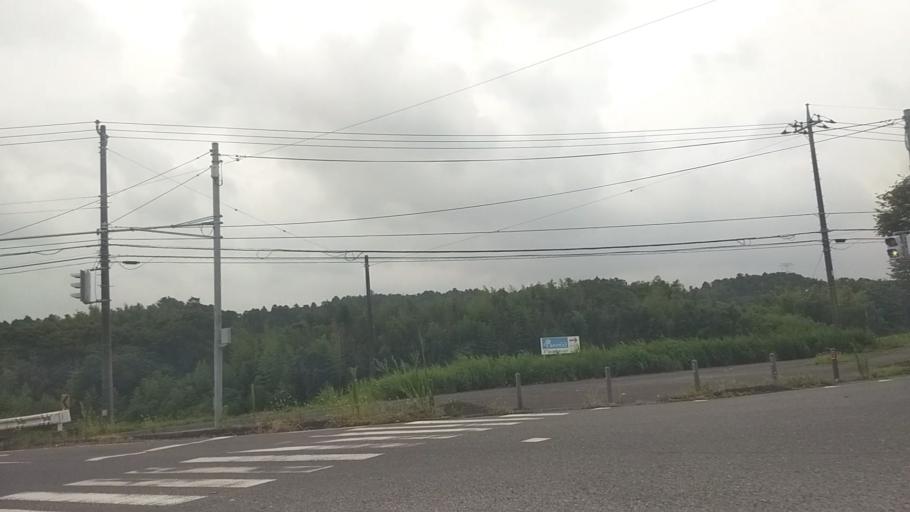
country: JP
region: Chiba
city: Kisarazu
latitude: 35.3745
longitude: 140.0125
